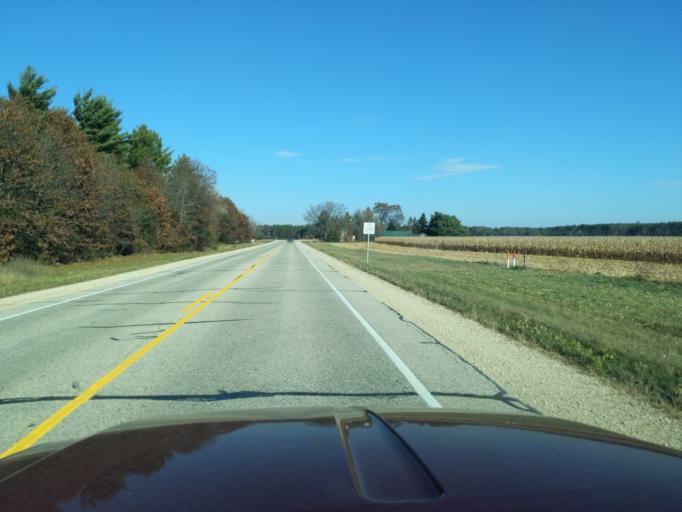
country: US
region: Wisconsin
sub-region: Waushara County
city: Wautoma
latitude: 44.0401
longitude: -89.2974
